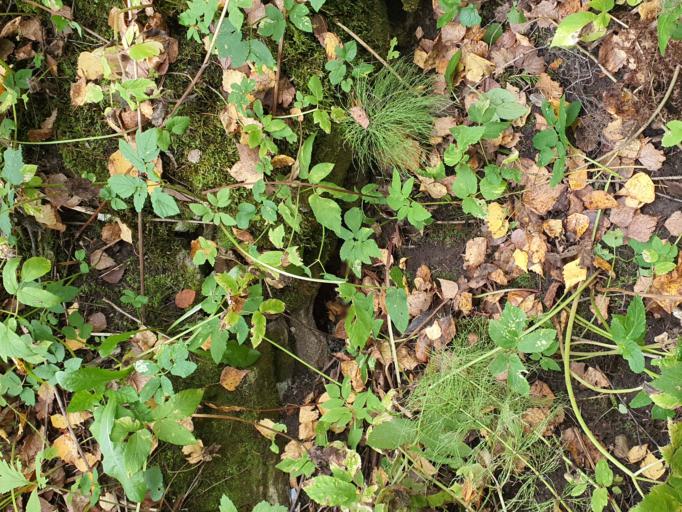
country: RU
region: St.-Petersburg
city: Tyarlevo
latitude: 59.6943
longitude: 30.4472
